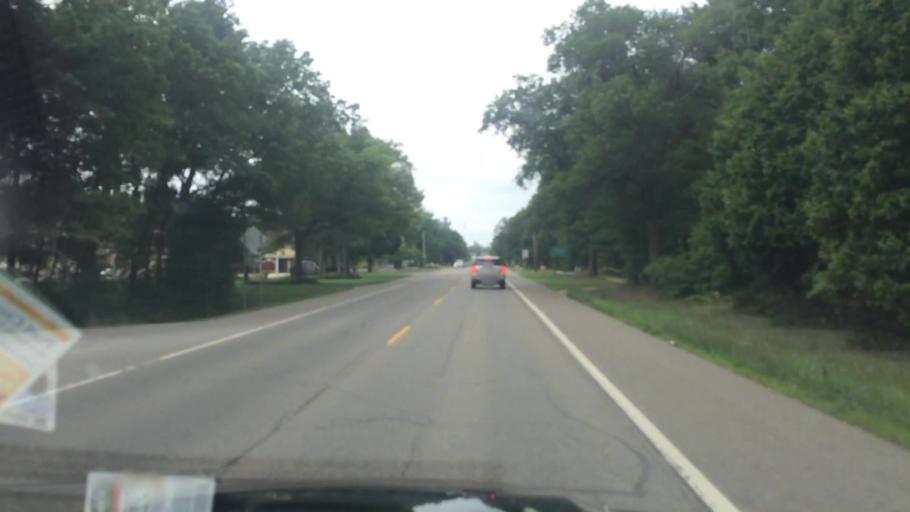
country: US
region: Michigan
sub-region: Huron County
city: Pigeon
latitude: 43.9536
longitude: -83.2666
